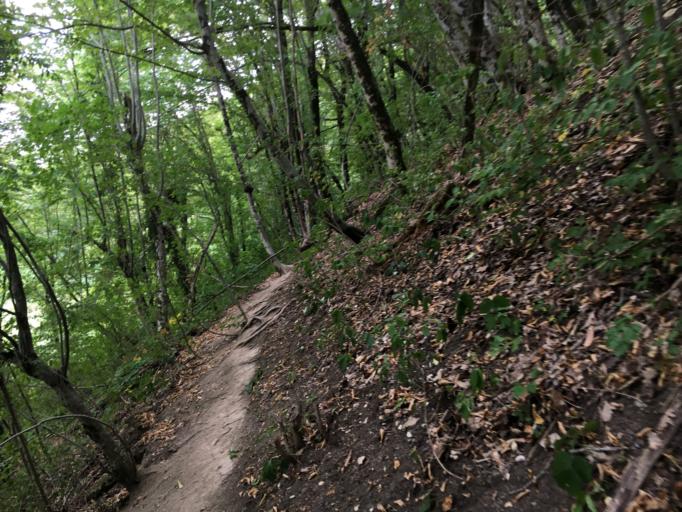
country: RU
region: Krasnodarskiy
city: Tuapse
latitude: 44.2526
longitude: 39.2289
